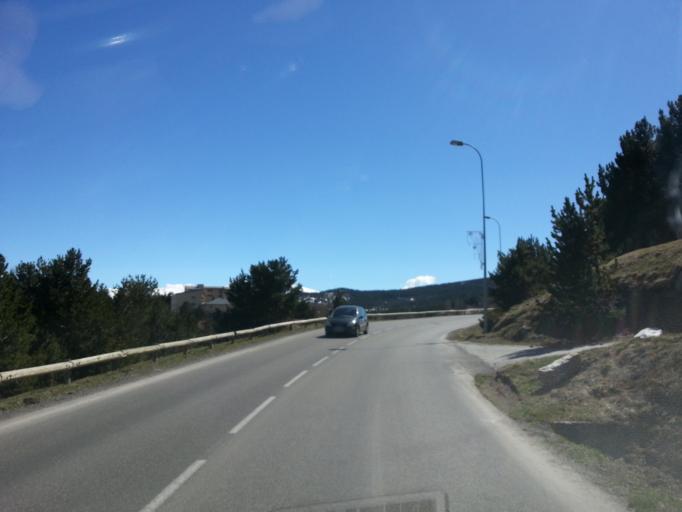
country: ES
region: Catalonia
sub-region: Provincia de Girona
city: Llivia
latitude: 42.5703
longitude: 2.0740
